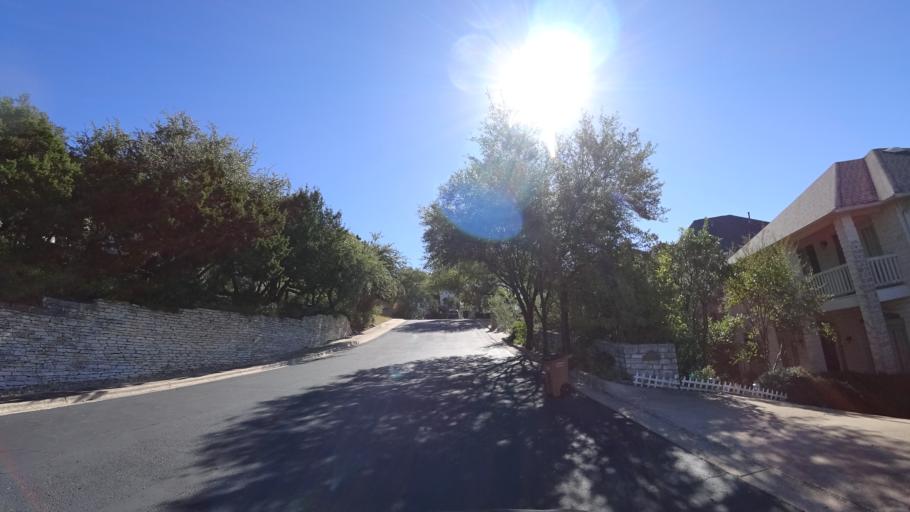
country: US
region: Texas
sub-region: Travis County
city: West Lake Hills
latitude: 30.3604
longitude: -97.7778
